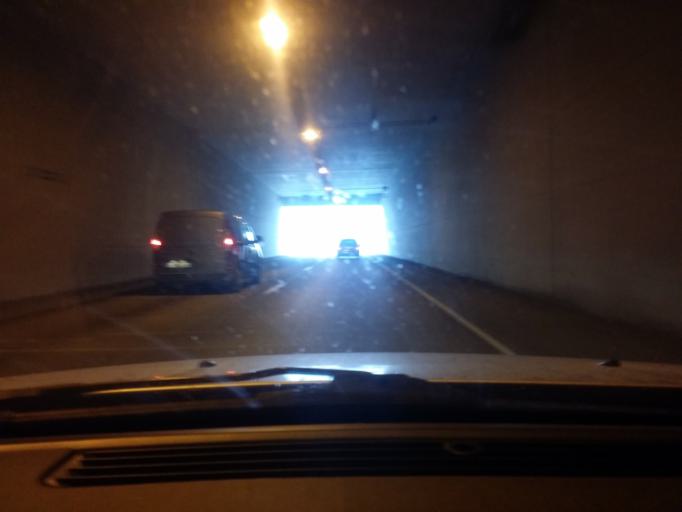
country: SE
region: Stockholm
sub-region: Stockholms Kommun
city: Kista
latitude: 59.3992
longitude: 17.8998
